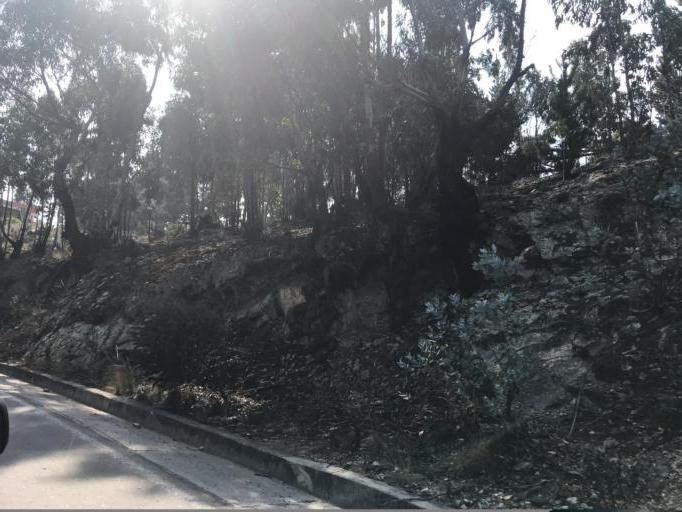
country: CO
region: Boyaca
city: Samaca
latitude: 5.4863
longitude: -73.4795
